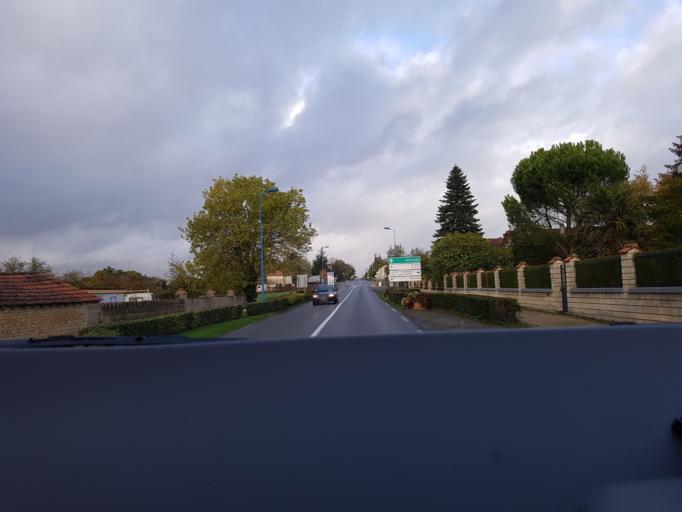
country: FR
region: Poitou-Charentes
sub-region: Departement des Deux-Sevres
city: Brioux-sur-Boutonne
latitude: 46.1508
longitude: -0.2124
